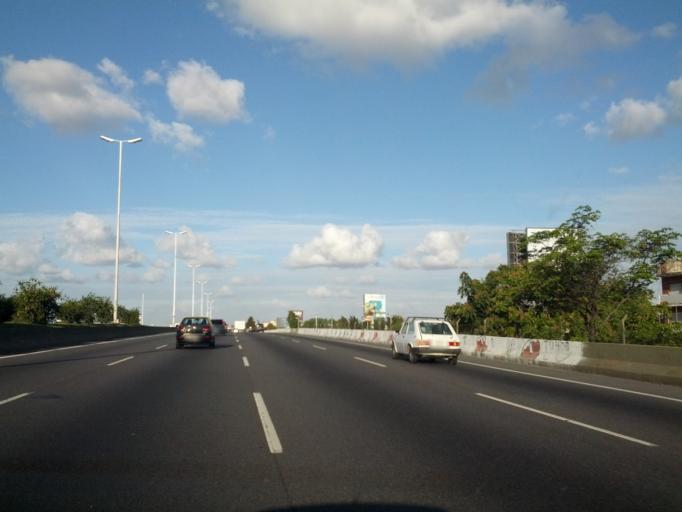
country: AR
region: Buenos Aires
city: Caseros
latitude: -34.6313
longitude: -58.5766
